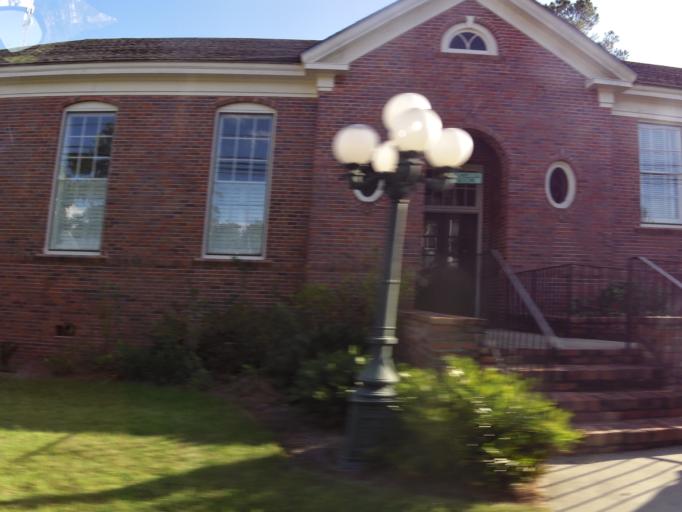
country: US
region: Georgia
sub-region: Brooks County
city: Quitman
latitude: 30.7858
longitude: -83.5588
